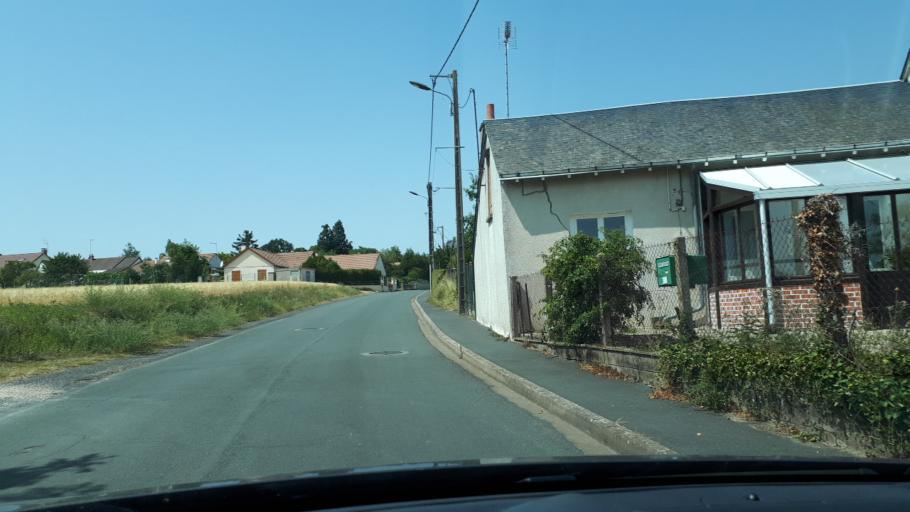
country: FR
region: Centre
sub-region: Departement du Loir-et-Cher
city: Vendome
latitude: 47.8132
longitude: 1.0633
